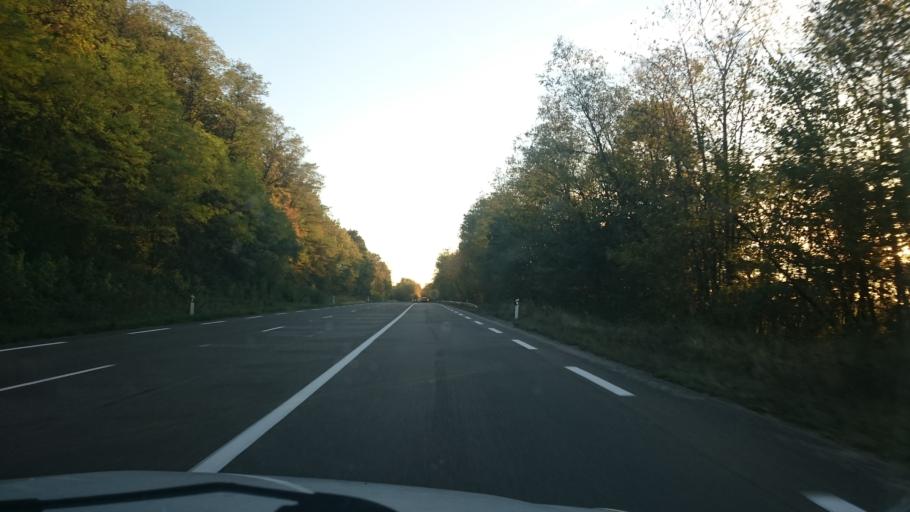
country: FR
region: Franche-Comte
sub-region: Departement du Jura
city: Mouchard
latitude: 46.9640
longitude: 5.7944
